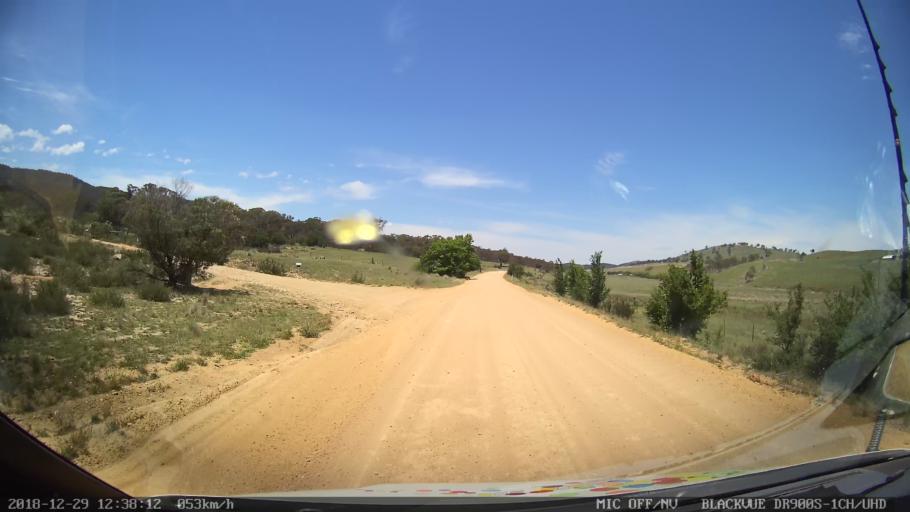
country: AU
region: Australian Capital Territory
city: Macarthur
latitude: -35.5867
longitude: 149.2292
